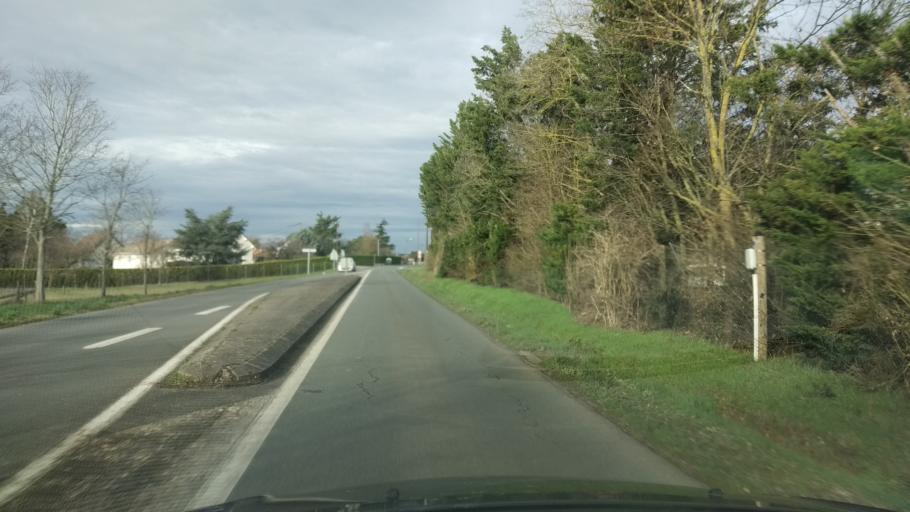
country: FR
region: Poitou-Charentes
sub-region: Departement de la Vienne
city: Saint-Georges-les-Baillargeaux
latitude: 46.6864
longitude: 0.4156
